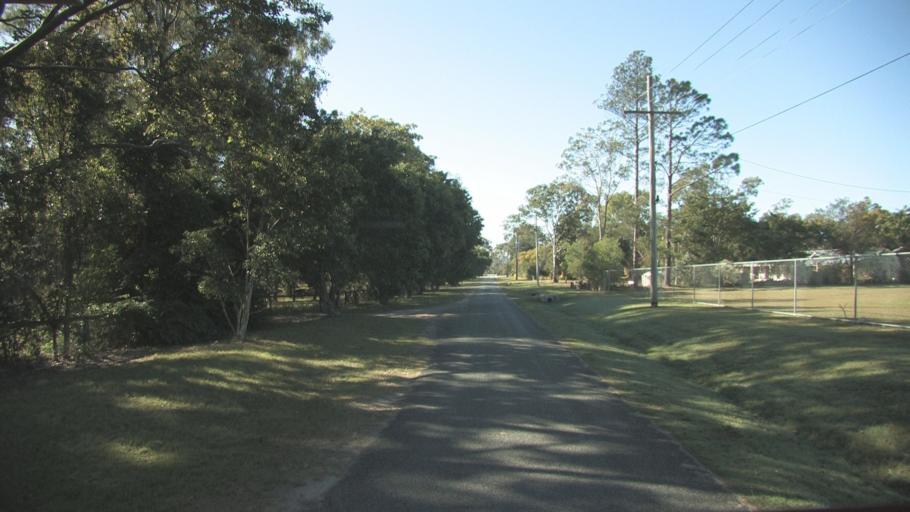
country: AU
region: Queensland
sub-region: Logan
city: North Maclean
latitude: -27.7637
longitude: 153.0423
